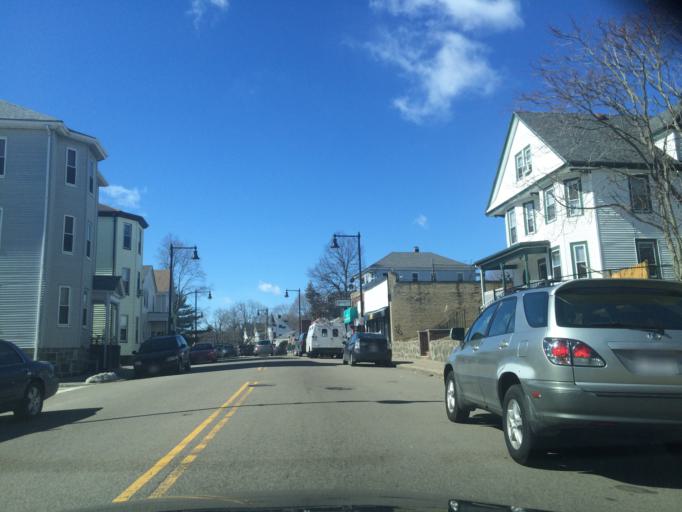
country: US
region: Massachusetts
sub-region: Suffolk County
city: Jamaica Plain
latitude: 42.2611
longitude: -71.1141
